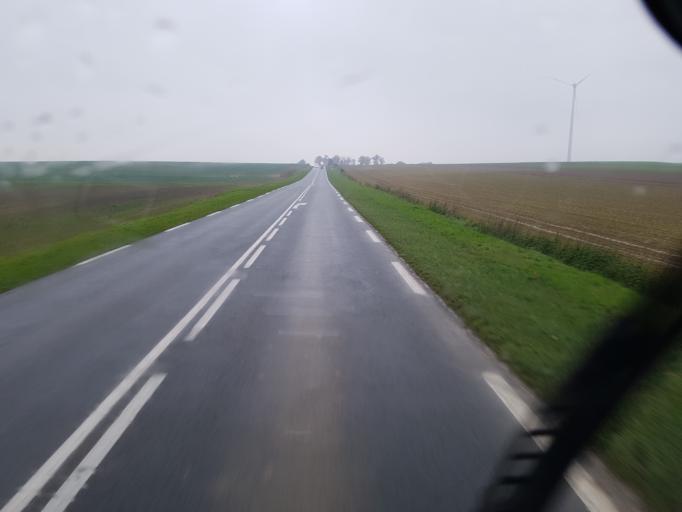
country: FR
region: Picardie
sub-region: Departement de l'Aisne
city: Omissy
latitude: 49.9002
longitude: 3.2619
